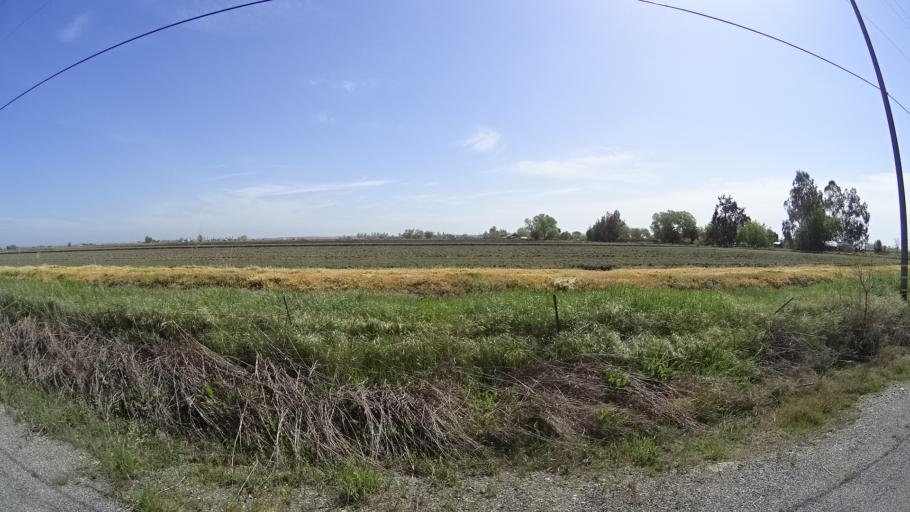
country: US
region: California
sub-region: Glenn County
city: Willows
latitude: 39.5844
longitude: -122.0556
